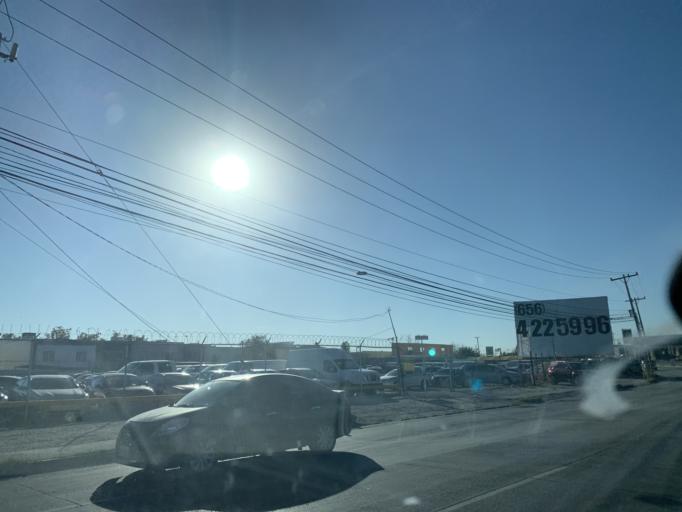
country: MX
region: Chihuahua
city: Ciudad Juarez
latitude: 31.6779
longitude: -106.4086
